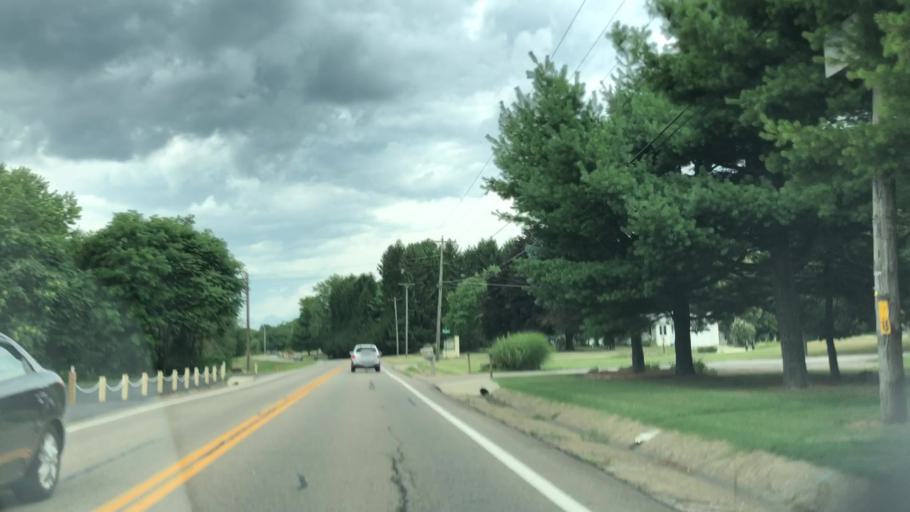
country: US
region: Ohio
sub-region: Summit County
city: Green
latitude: 40.9474
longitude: -81.4913
